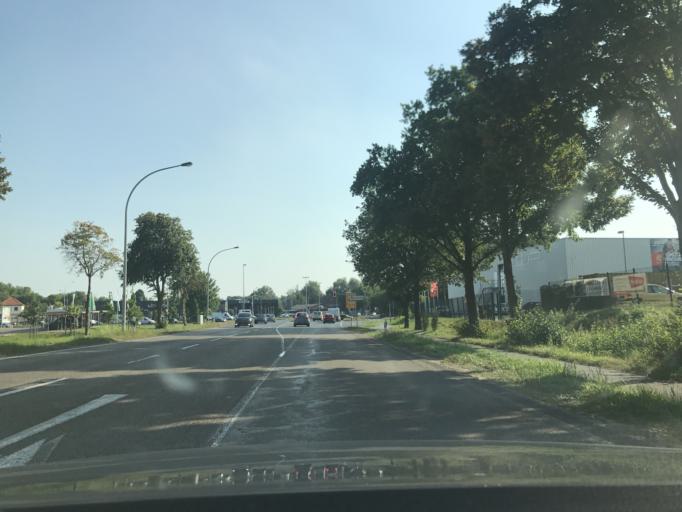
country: DE
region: North Rhine-Westphalia
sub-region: Regierungsbezirk Dusseldorf
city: Kleve
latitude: 51.8019
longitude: 6.1384
